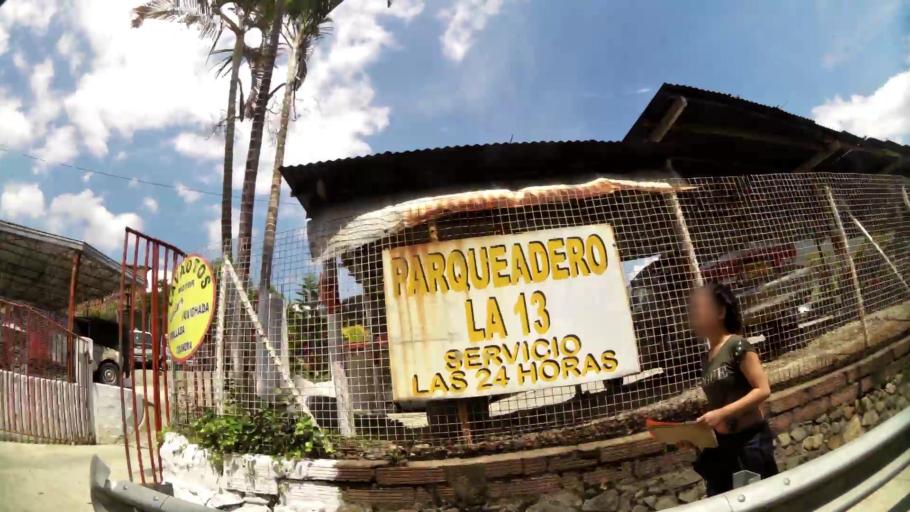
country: CO
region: Antioquia
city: La Estrella
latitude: 6.1863
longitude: -75.6502
